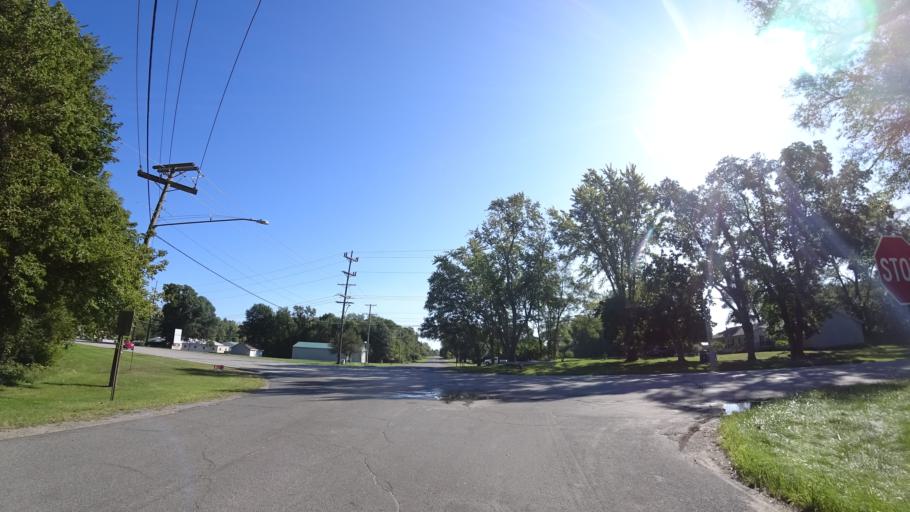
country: US
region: Michigan
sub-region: Berrien County
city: Bridgman
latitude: 41.9683
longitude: -86.5487
